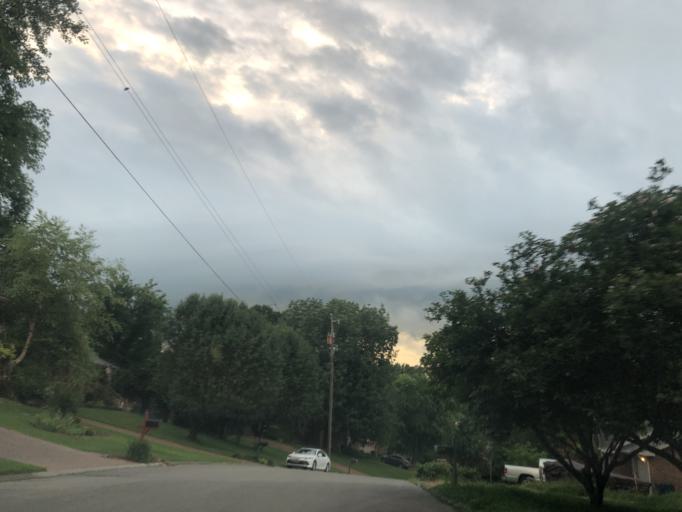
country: US
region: Tennessee
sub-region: Davidson County
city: Lakewood
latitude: 36.1474
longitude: -86.6333
